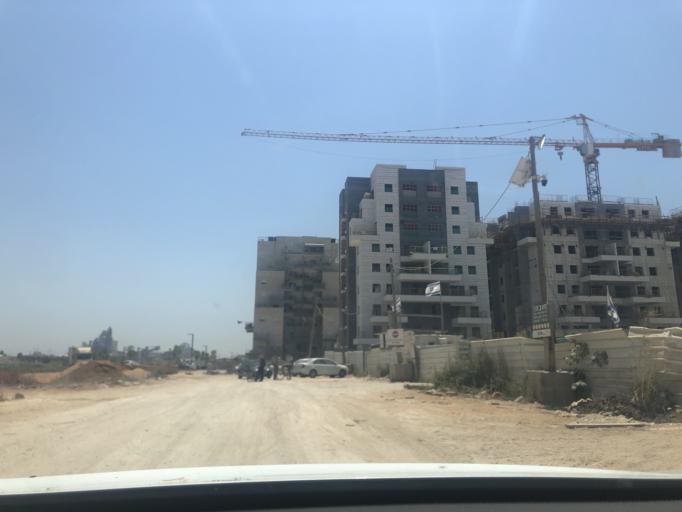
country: IL
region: Central District
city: Lod
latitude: 31.9381
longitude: 34.9007
